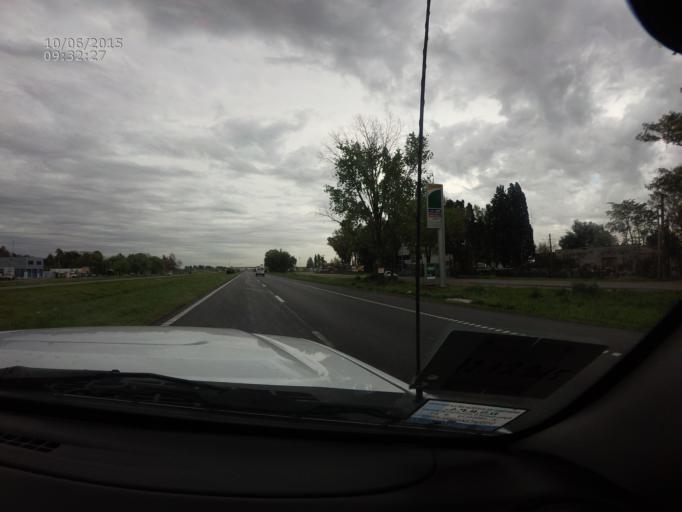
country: AR
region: Buenos Aires
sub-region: Partido de Zarate
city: Zarate
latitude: -34.1270
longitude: -59.0795
